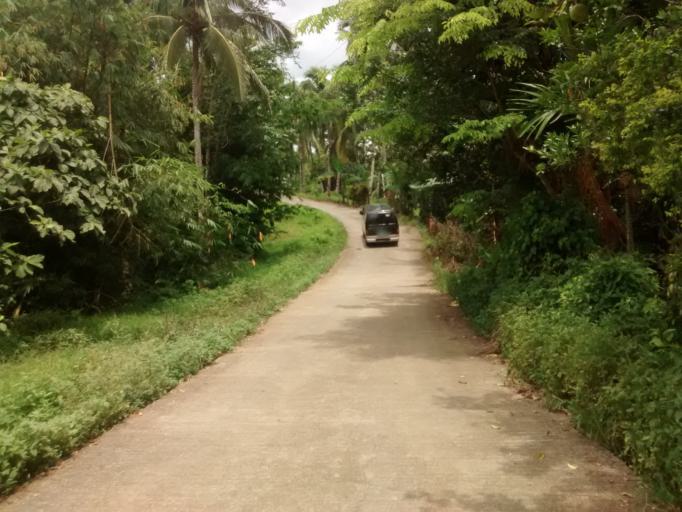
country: PH
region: Calabarzon
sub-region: Province of Quezon
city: Lucban
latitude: 14.1562
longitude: 121.5538
